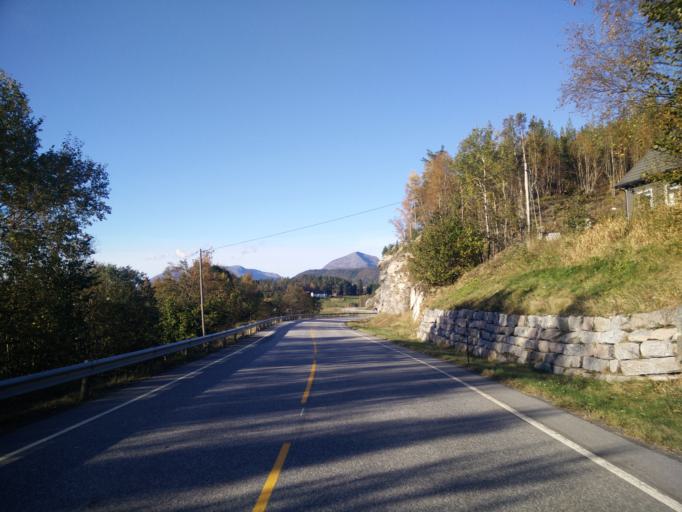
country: NO
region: More og Romsdal
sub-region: Halsa
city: Liaboen
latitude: 63.0957
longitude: 8.3473
